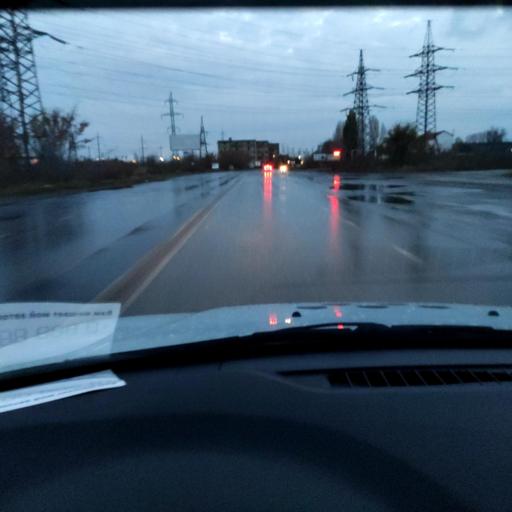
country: RU
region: Samara
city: Tol'yatti
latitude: 53.5176
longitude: 49.4657
